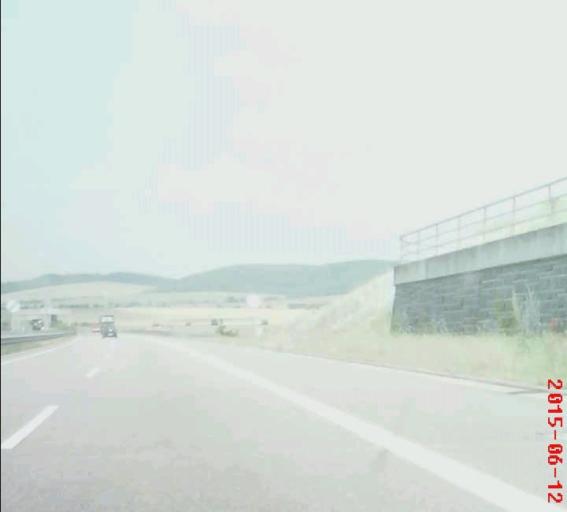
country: DE
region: Thuringia
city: Heldrungen
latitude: 51.2834
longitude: 11.2257
